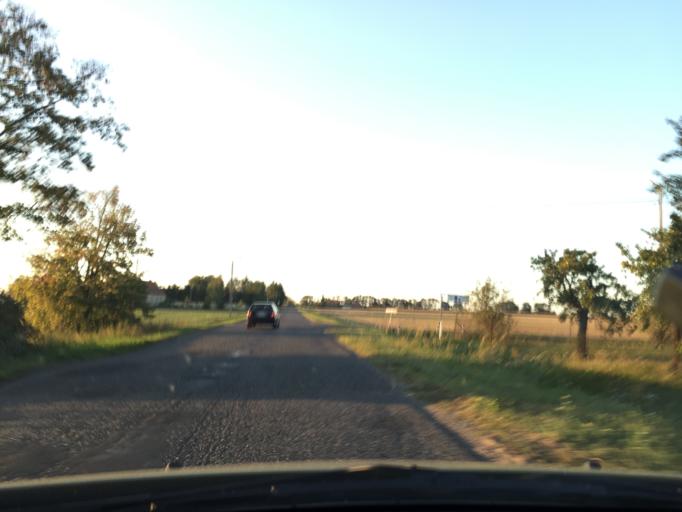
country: PL
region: Greater Poland Voivodeship
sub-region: Powiat pleszewski
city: Dobrzyca
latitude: 51.8250
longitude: 17.6203
